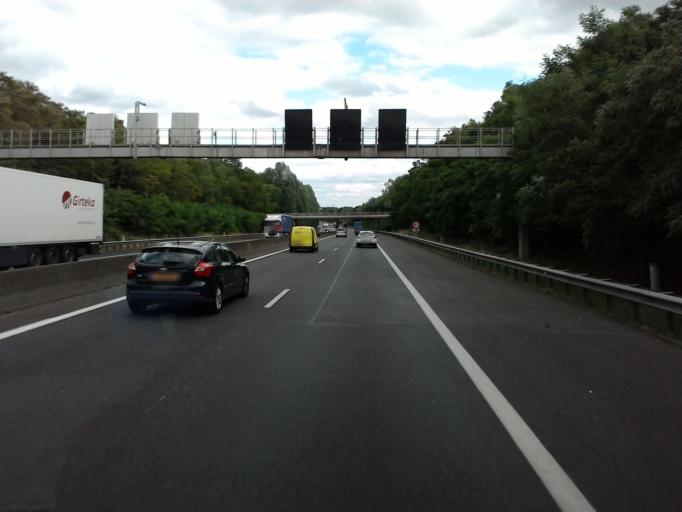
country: LU
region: Luxembourg
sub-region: Canton de Capellen
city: Mamer
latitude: 49.6349
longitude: 6.0291
